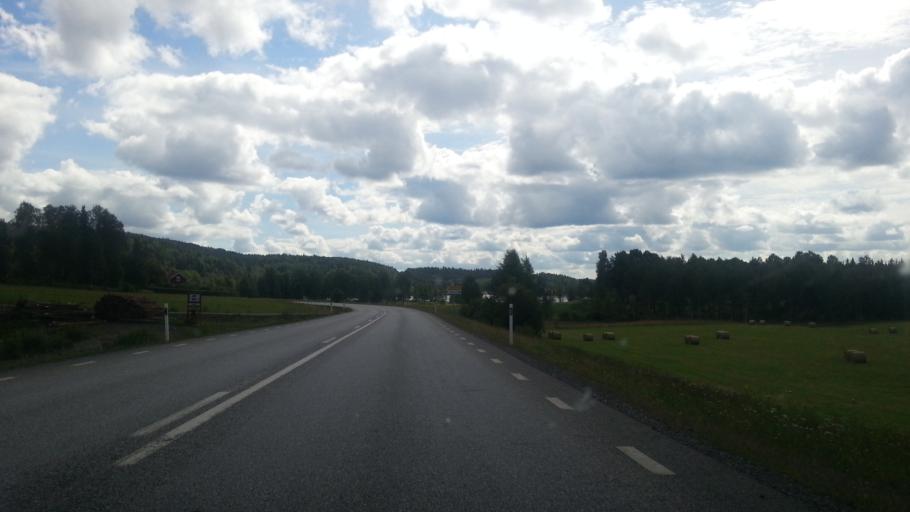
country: SE
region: OErebro
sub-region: Ljusnarsbergs Kommun
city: Kopparberg
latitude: 59.8360
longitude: 15.0975
